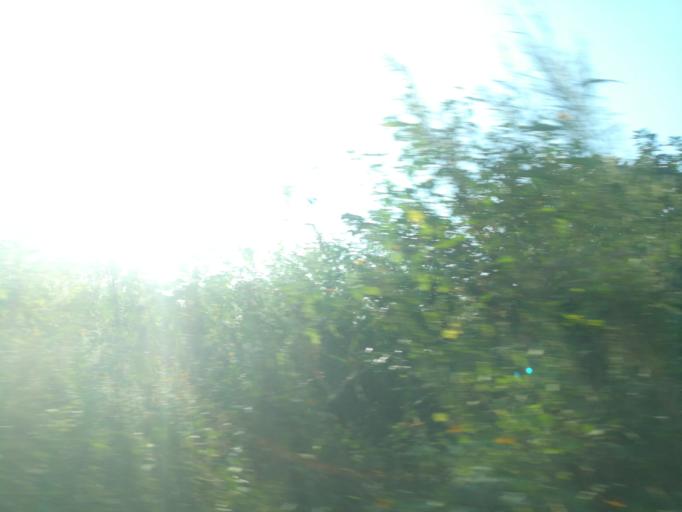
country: NG
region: Ogun
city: Abeokuta
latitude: 7.2368
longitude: 3.3008
